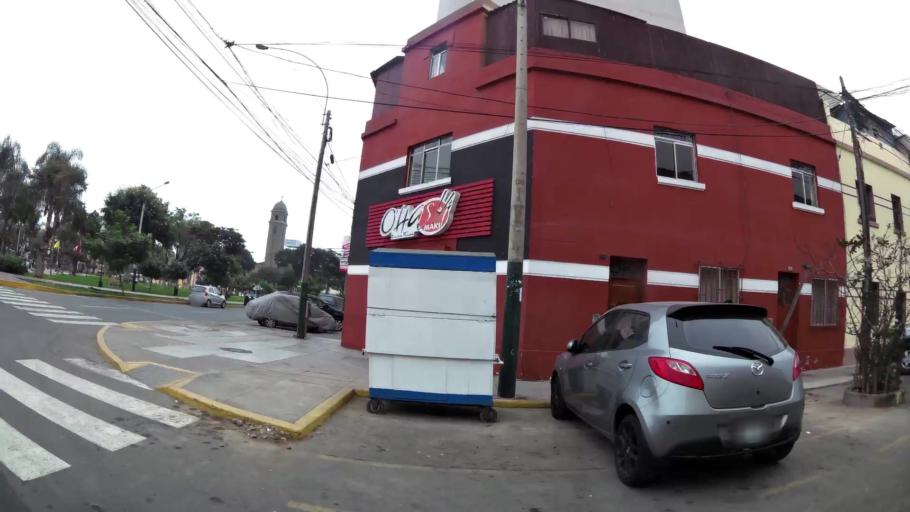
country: PE
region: Lima
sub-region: Lima
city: San Luis
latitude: -12.0817
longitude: -77.0306
